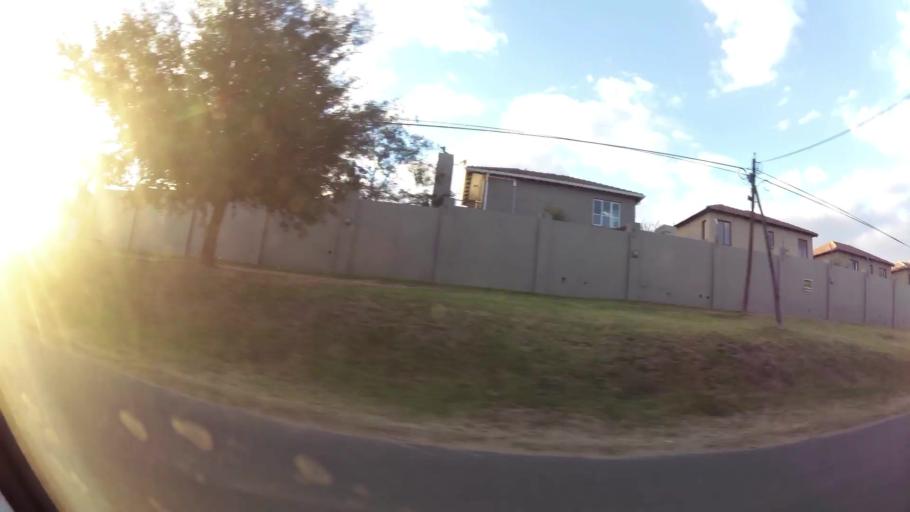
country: ZA
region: Gauteng
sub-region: City of Johannesburg Metropolitan Municipality
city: Diepsloot
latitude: -26.0169
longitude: 27.9851
